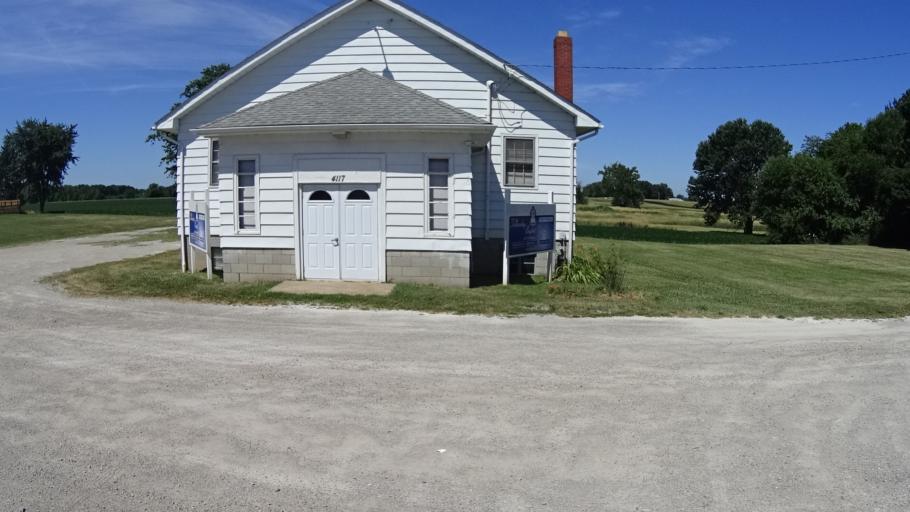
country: US
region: Ohio
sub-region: Erie County
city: Sandusky
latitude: 41.4074
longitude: -82.7027
